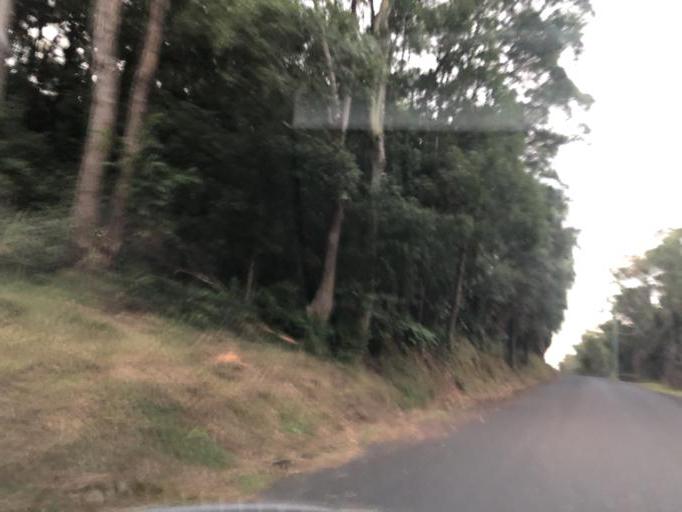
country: AU
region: New South Wales
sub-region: Coffs Harbour
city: Coffs Harbour
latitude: -30.3093
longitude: 153.1296
